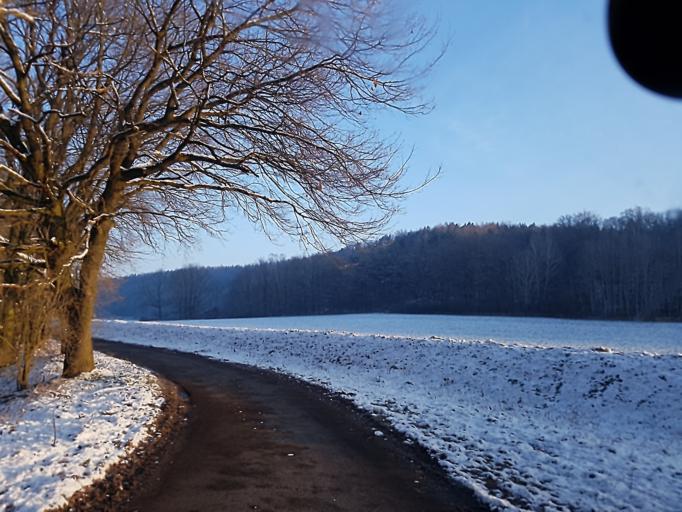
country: DE
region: Saxony
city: Grossweitzschen
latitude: 51.1474
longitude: 13.0110
